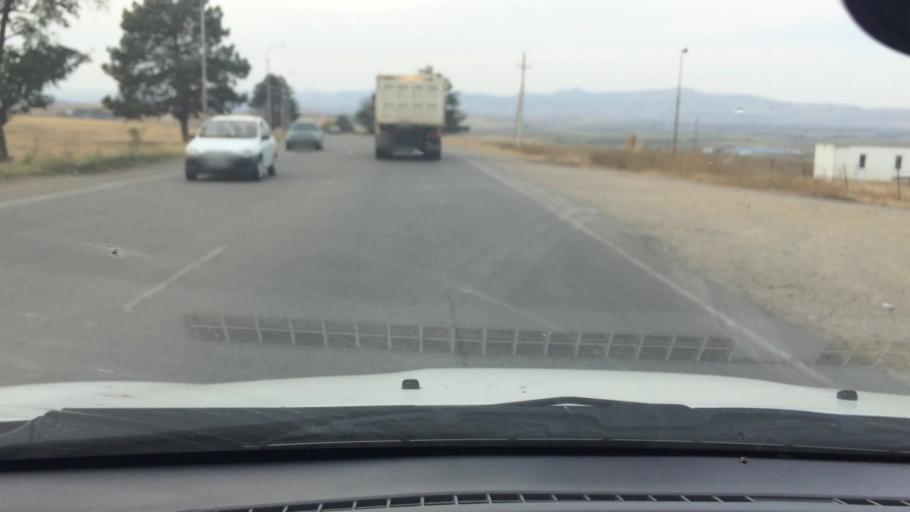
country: GE
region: Kvemo Kartli
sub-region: Marneuli
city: Marneuli
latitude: 41.5130
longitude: 44.7894
